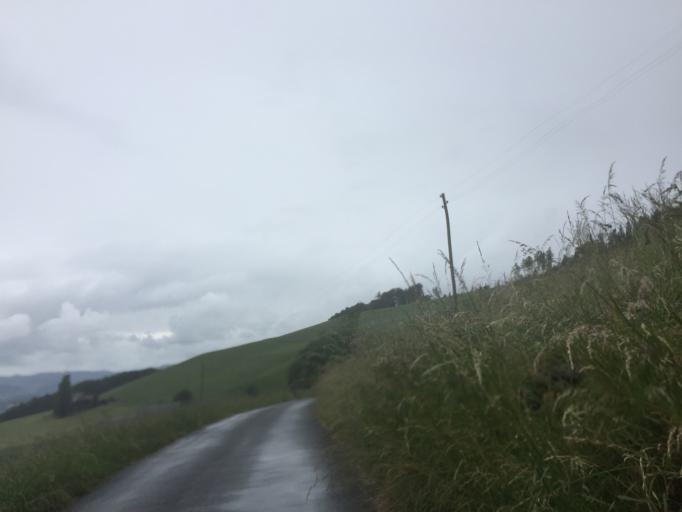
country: CH
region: Bern
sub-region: Bern-Mittelland District
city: Taegertschi
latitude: 46.8897
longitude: 7.6003
